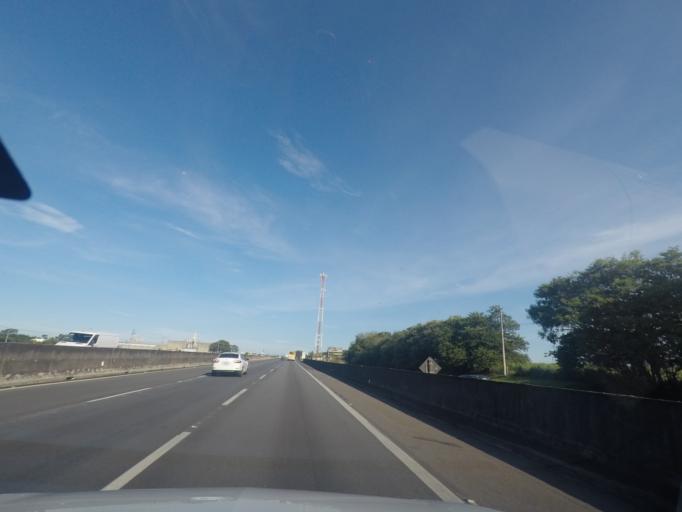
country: BR
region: Sao Paulo
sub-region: Nova Odessa
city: Nova Odessa
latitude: -22.7393
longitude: -47.2746
